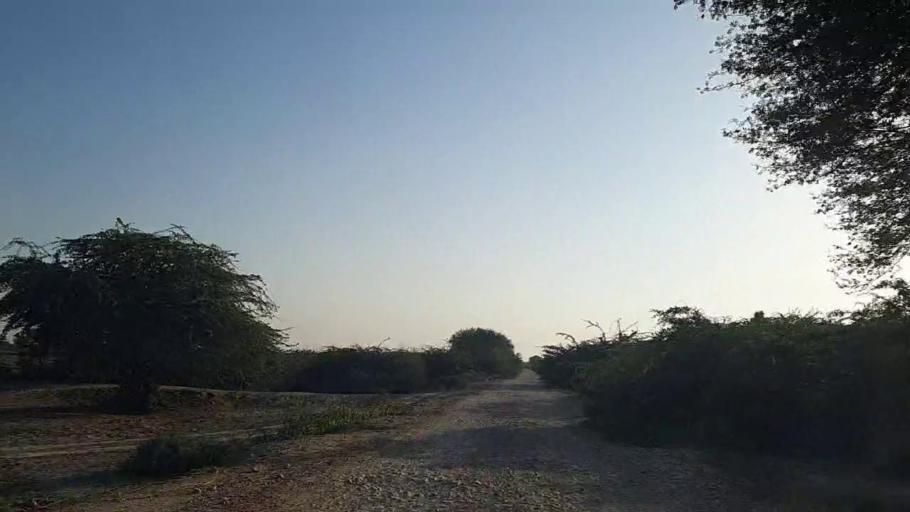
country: PK
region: Sindh
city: Jati
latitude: 24.4272
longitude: 68.1892
